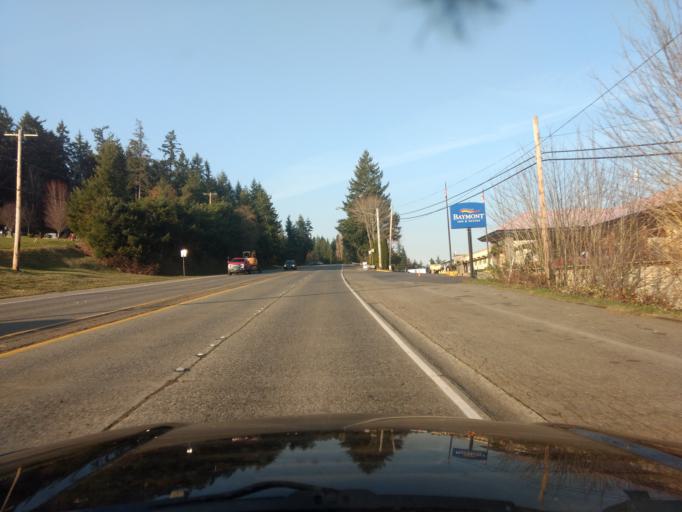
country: US
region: Washington
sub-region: Kitsap County
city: Erlands Point-Kitsap Lake
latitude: 47.5733
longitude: -122.6887
